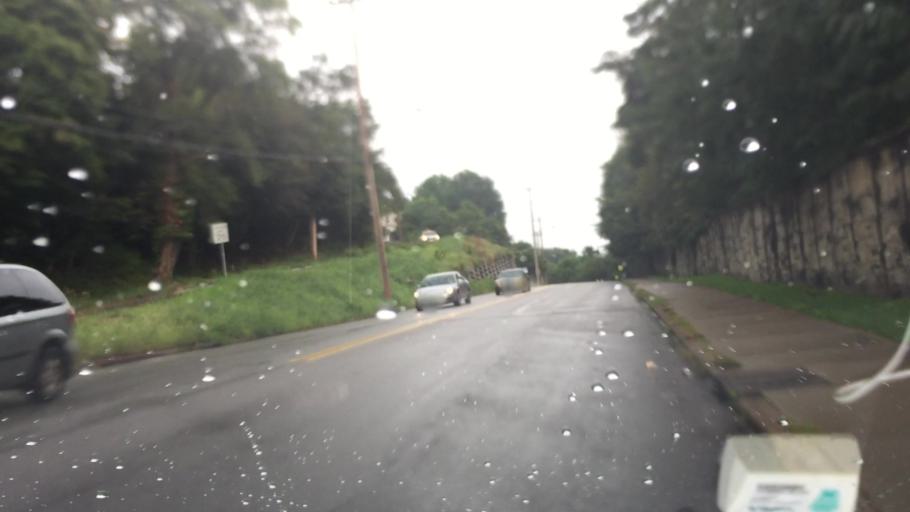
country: US
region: Pennsylvania
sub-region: Allegheny County
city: Bloomfield
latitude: 40.4782
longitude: -79.9490
